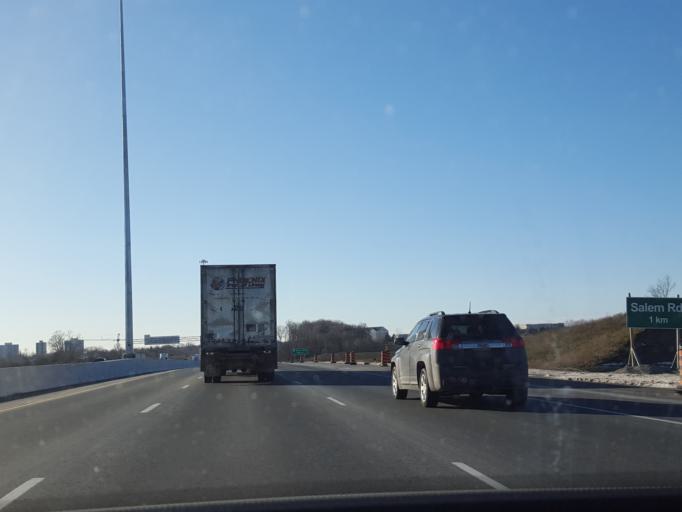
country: CA
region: Ontario
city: Ajax
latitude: 43.8594
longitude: -78.9951
